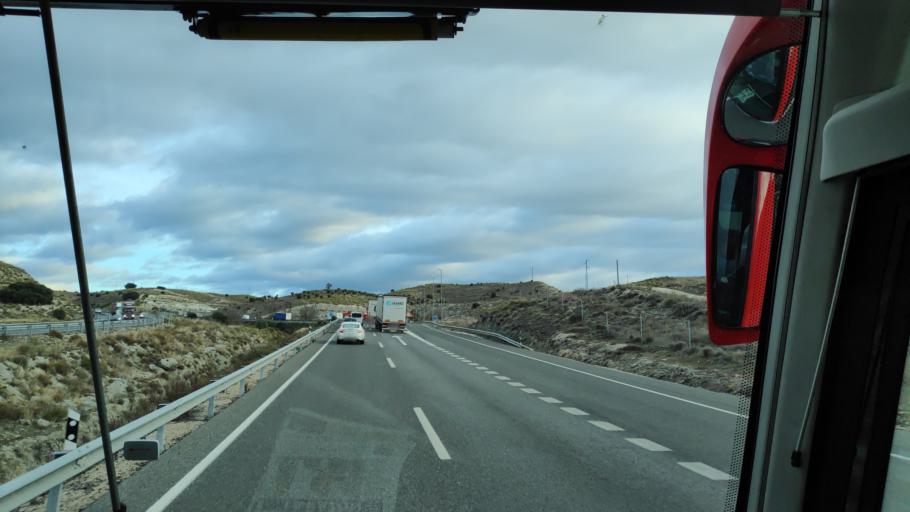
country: ES
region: Madrid
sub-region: Provincia de Madrid
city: Perales de Tajuna
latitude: 40.2096
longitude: -3.3225
